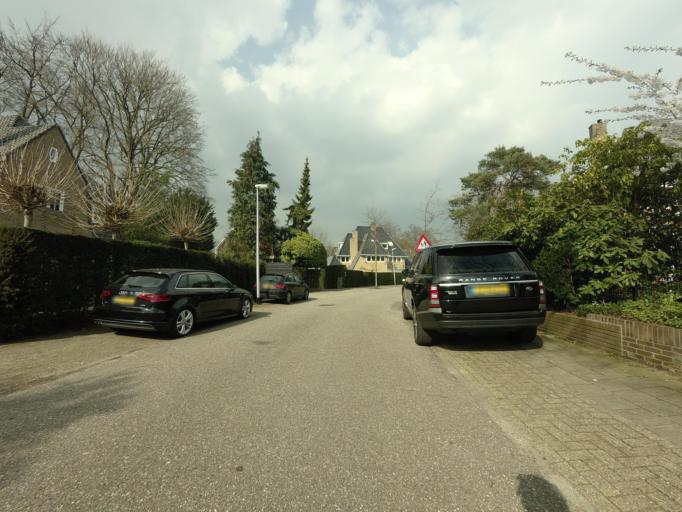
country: NL
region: North Holland
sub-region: Gemeente Bussum
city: Bussum
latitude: 52.2815
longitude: 5.1767
